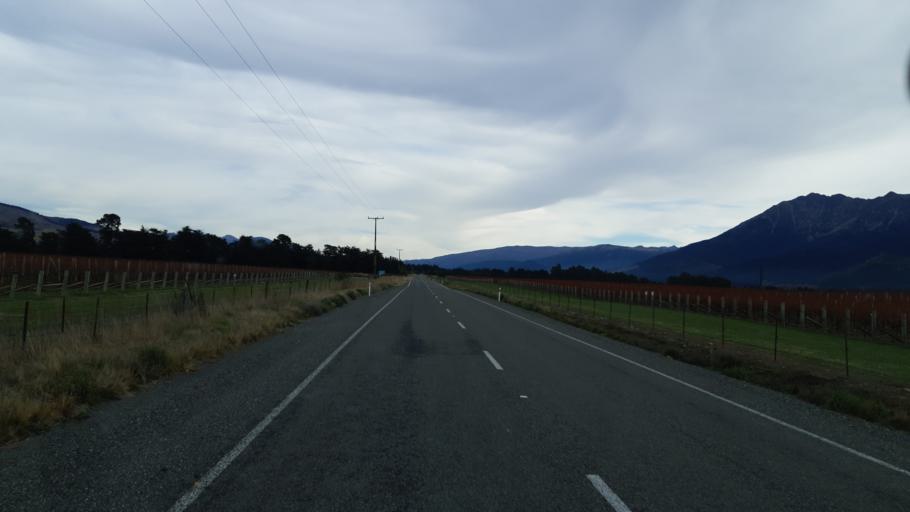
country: NZ
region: Tasman
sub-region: Tasman District
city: Richmond
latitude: -41.6241
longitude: 173.3523
